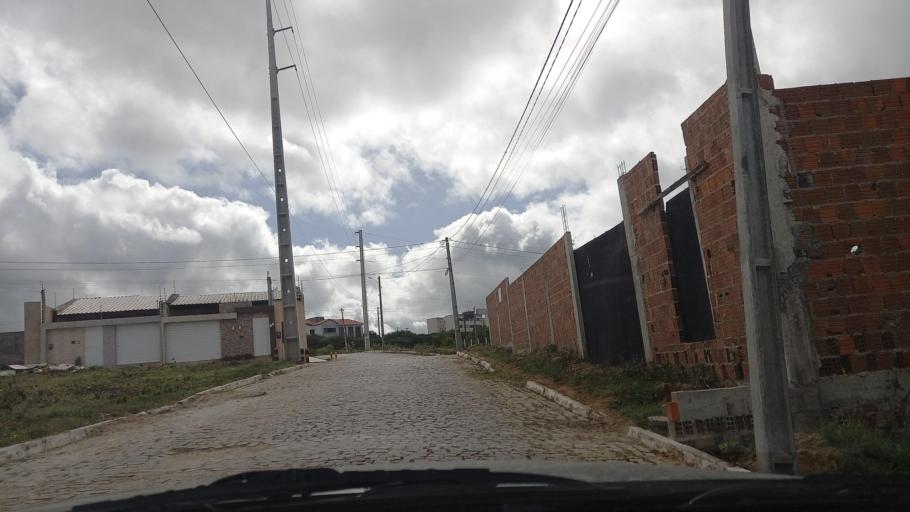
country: BR
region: Pernambuco
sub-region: Caruaru
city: Caruaru
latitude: -8.3051
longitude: -35.9542
